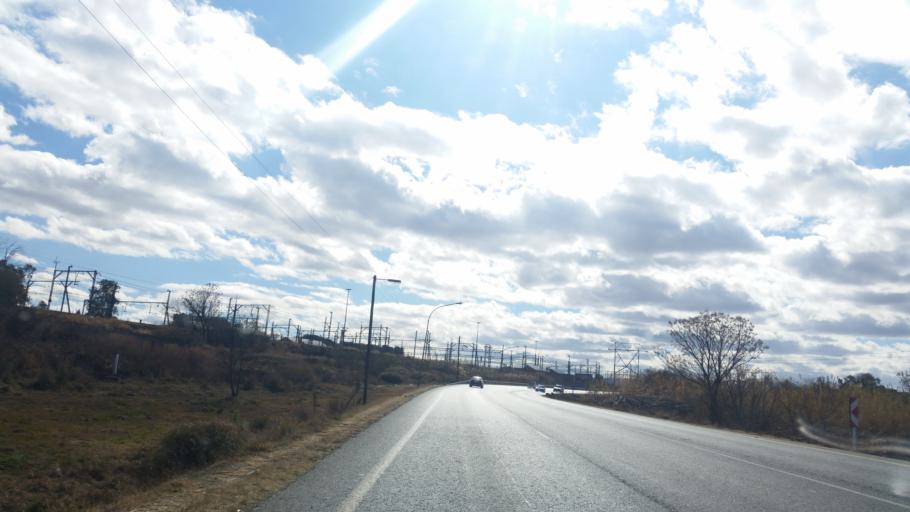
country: ZA
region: KwaZulu-Natal
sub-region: uThukela District Municipality
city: Ladysmith
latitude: -28.5461
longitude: 29.7943
